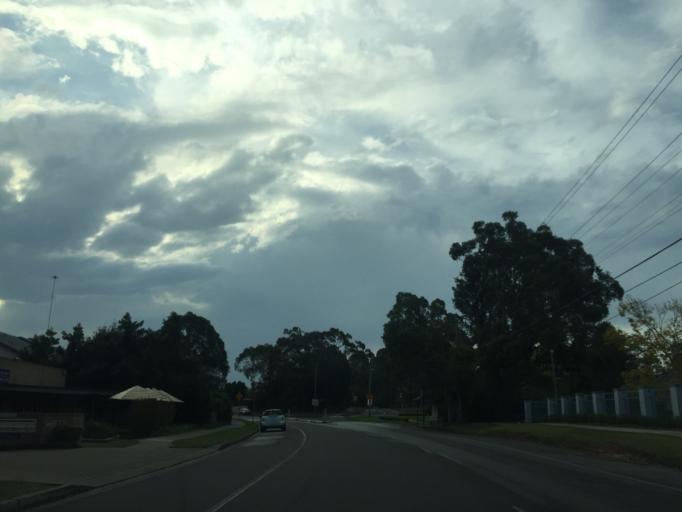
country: AU
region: New South Wales
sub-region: The Hills Shire
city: Glenhaven
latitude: -33.6982
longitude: 151.0017
